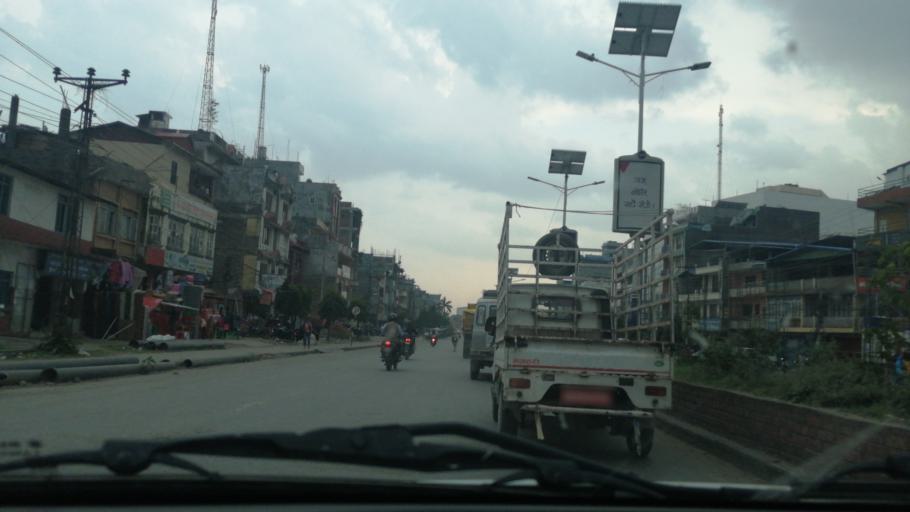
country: NP
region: Western Region
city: Butwal
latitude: 27.7006
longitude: 83.4660
